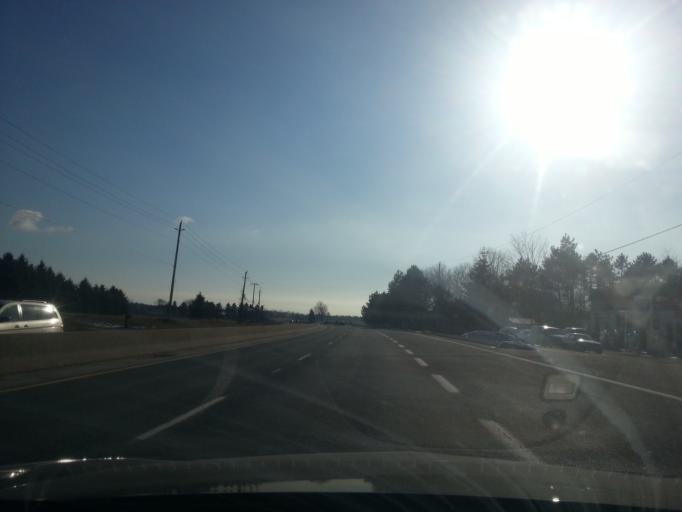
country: CA
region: Ontario
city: Oshawa
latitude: 43.9632
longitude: -78.6110
